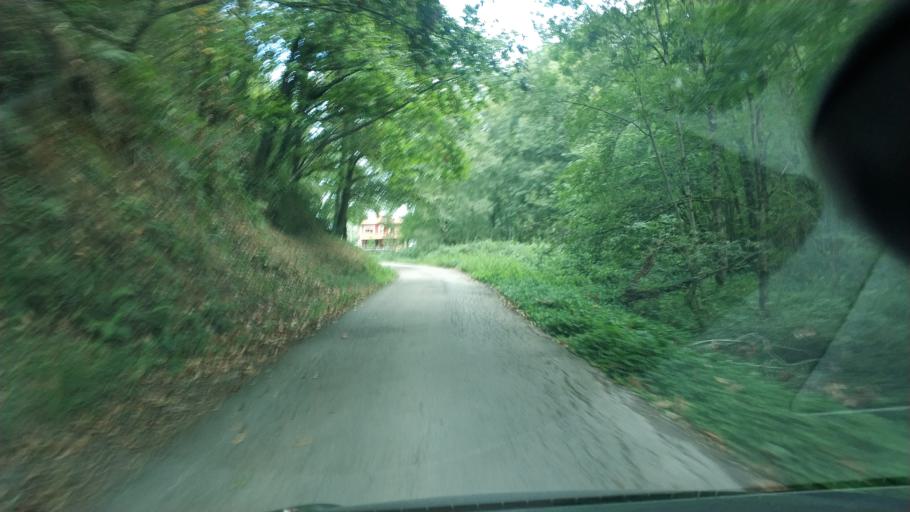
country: ES
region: Cantabria
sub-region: Provincia de Cantabria
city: Santa Maria de Cayon
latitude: 43.3005
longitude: -3.8557
